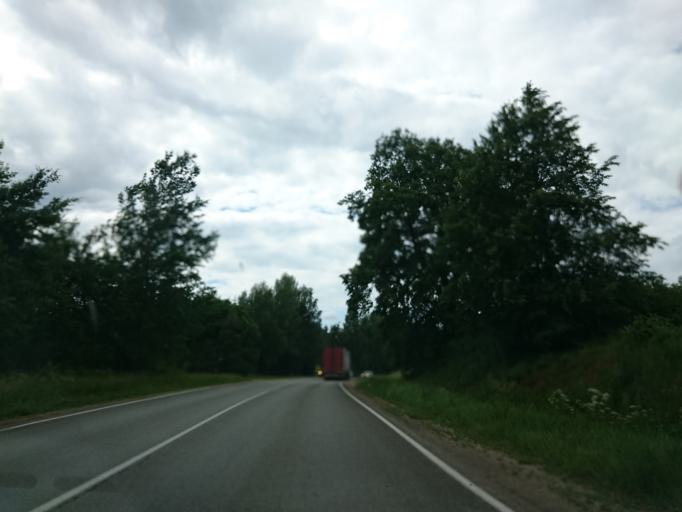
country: LV
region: Ludzas Rajons
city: Ludza
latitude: 56.5341
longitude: 27.5867
